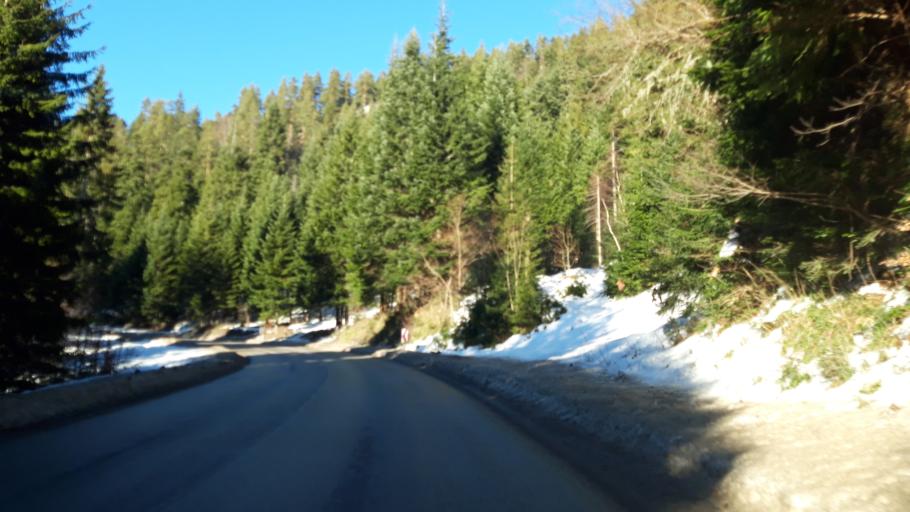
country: BA
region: Republika Srpska
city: Pale
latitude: 43.9192
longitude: 18.6539
